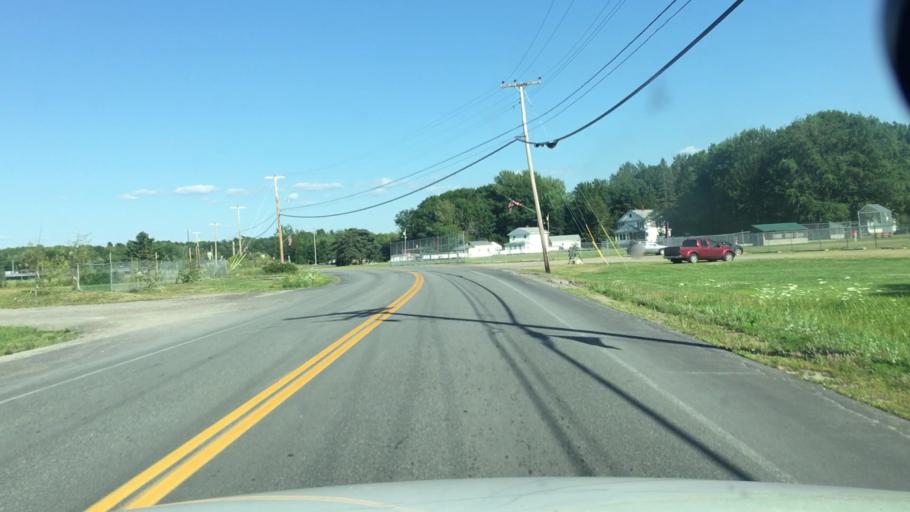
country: US
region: Maine
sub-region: Penobscot County
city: Howland
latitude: 45.2368
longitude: -68.6584
